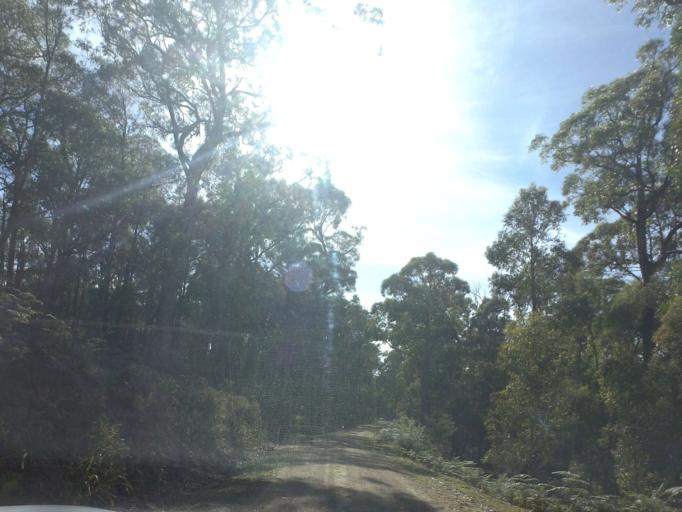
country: AU
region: Victoria
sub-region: Moorabool
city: Bacchus Marsh
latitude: -37.4303
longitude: 144.2389
